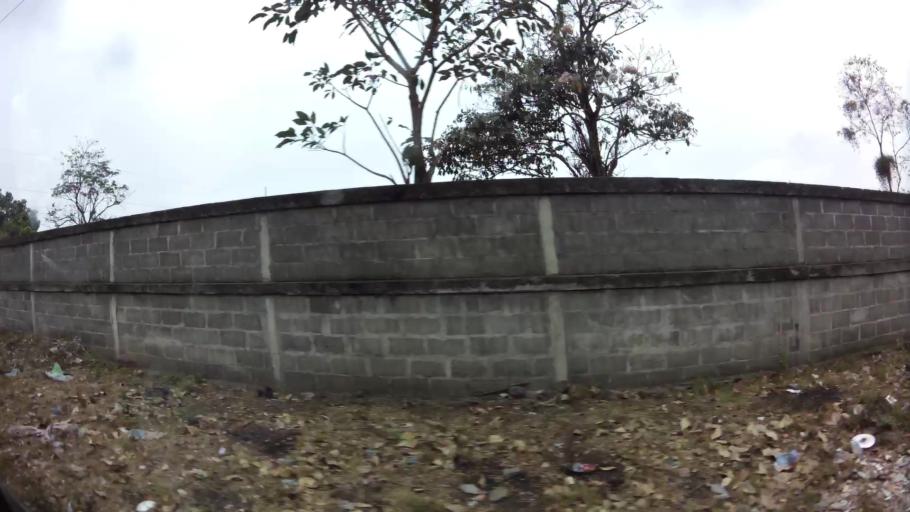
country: NI
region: Chinandega
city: Chinandega
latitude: 12.6178
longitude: -87.1139
